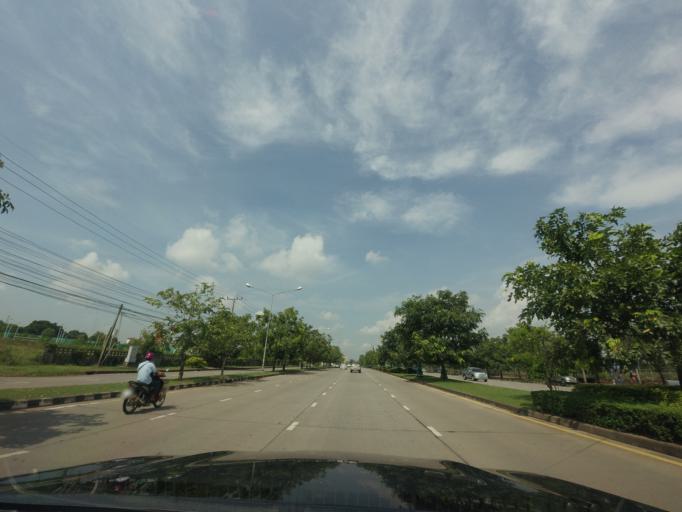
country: TH
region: Khon Kaen
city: Khon Kaen
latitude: 16.4421
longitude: 102.8112
